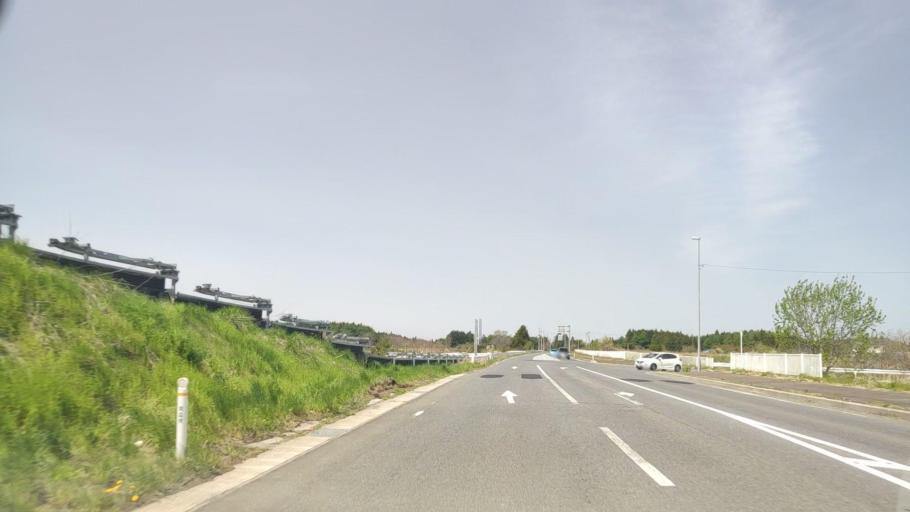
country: JP
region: Aomori
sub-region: Hachinohe Shi
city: Uchimaru
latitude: 40.5277
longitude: 141.4090
